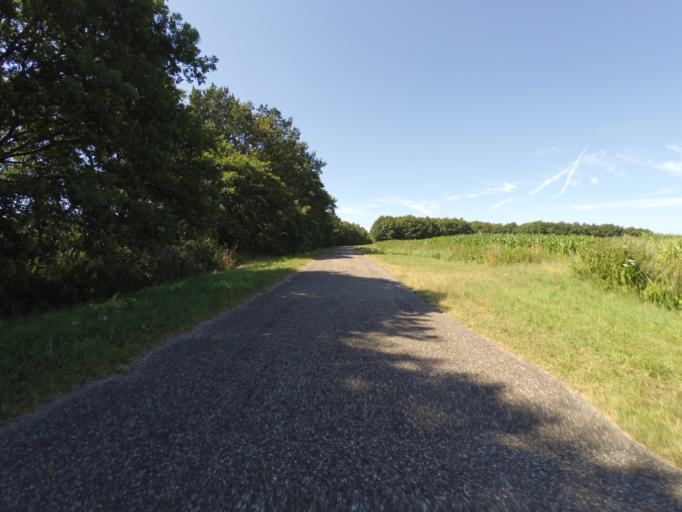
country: NL
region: Drenthe
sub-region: Gemeente Aa en Hunze
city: Anloo
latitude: 52.9683
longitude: 6.7039
